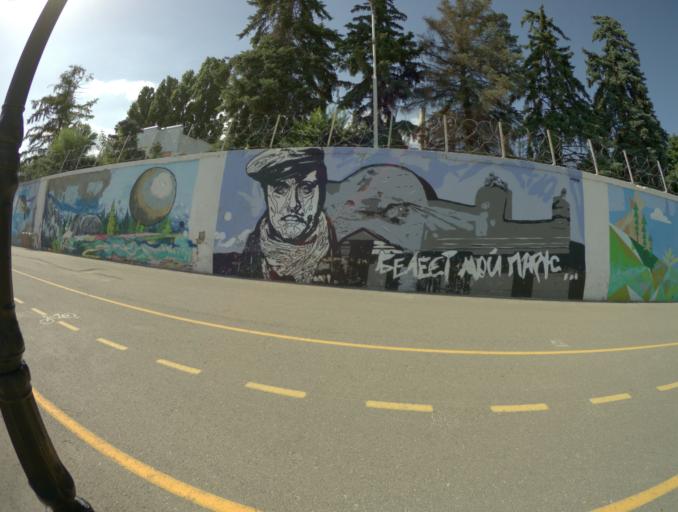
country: RU
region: Saratov
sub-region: Saratovskiy Rayon
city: Saratov
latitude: 51.5214
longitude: 46.0346
